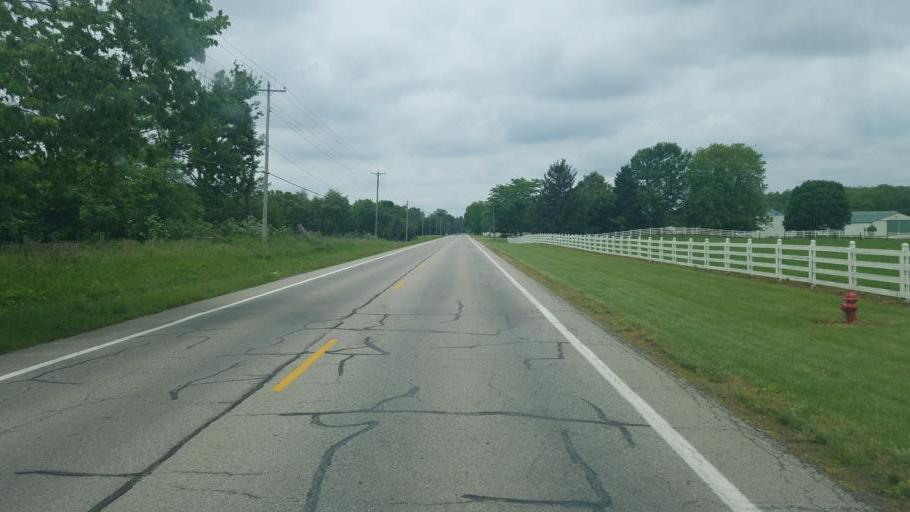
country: US
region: Ohio
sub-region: Fairfield County
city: Millersport
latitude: 39.9589
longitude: -82.5818
